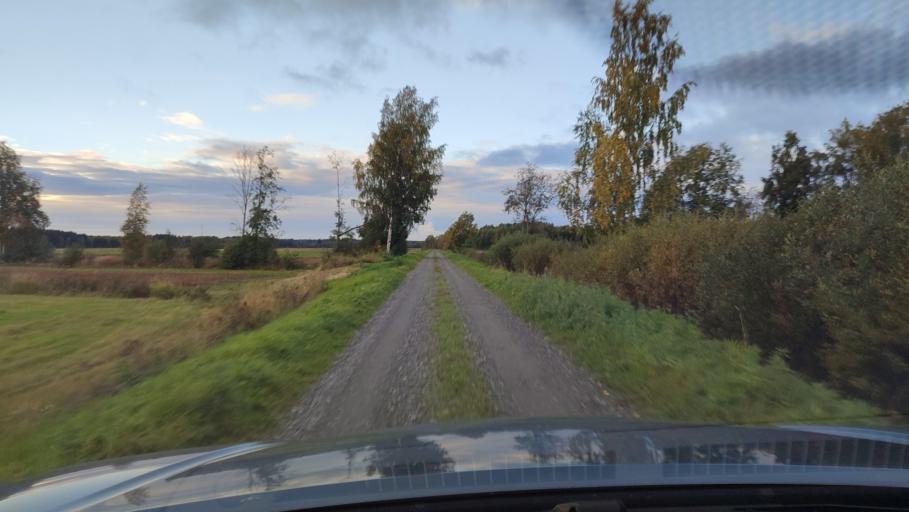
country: FI
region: Ostrobothnia
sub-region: Sydosterbotten
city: Kristinestad
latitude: 62.2400
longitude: 21.4551
